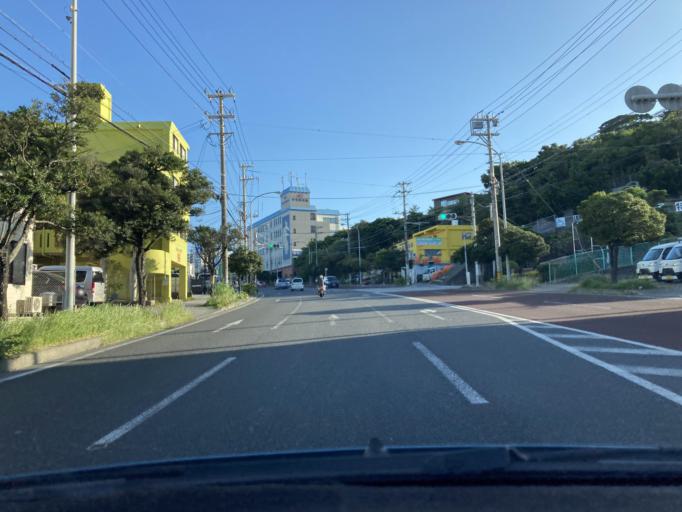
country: JP
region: Okinawa
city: Ginowan
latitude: 26.2456
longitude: 127.7375
